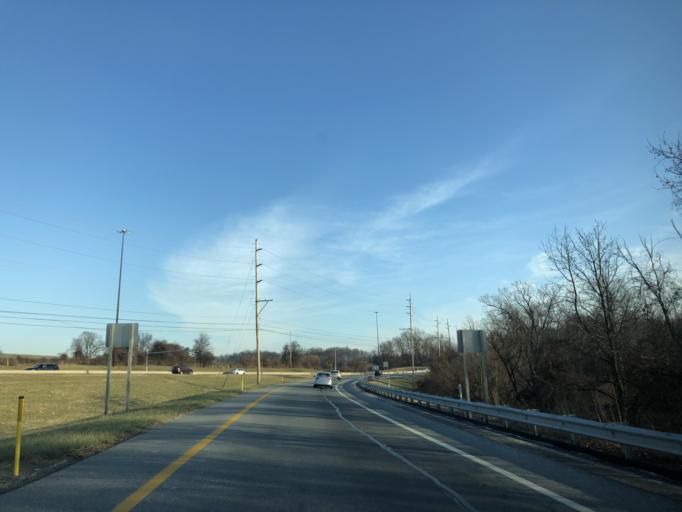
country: US
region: Pennsylvania
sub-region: Chester County
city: Exton
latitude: 40.0620
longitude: -75.6699
